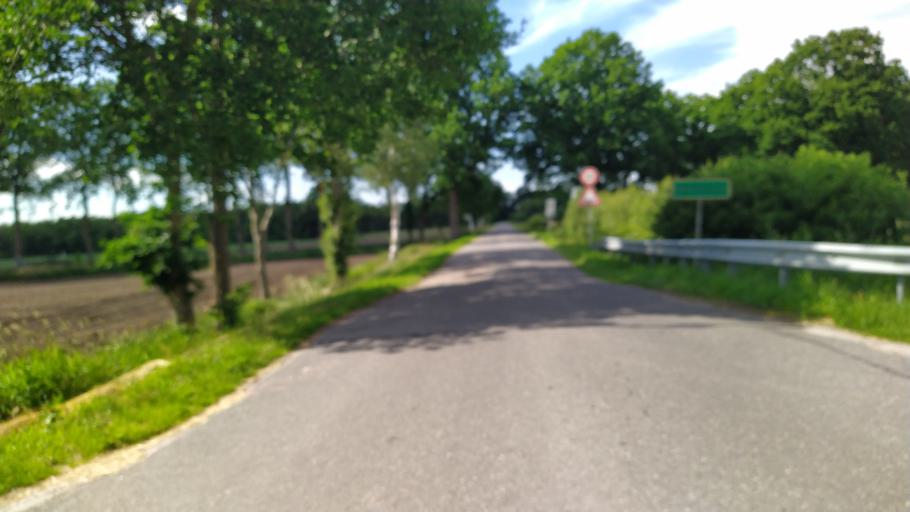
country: DE
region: Lower Saxony
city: Odisheim
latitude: 53.6543
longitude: 8.9362
